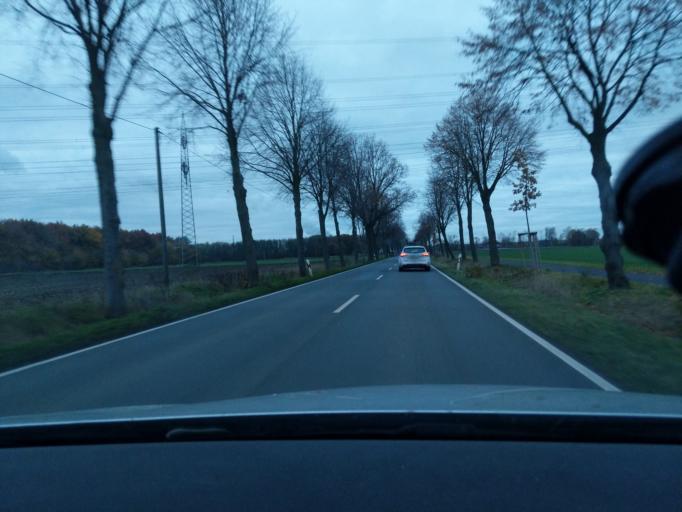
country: DE
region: North Rhine-Westphalia
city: Waltrop
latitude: 51.6514
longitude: 7.4260
